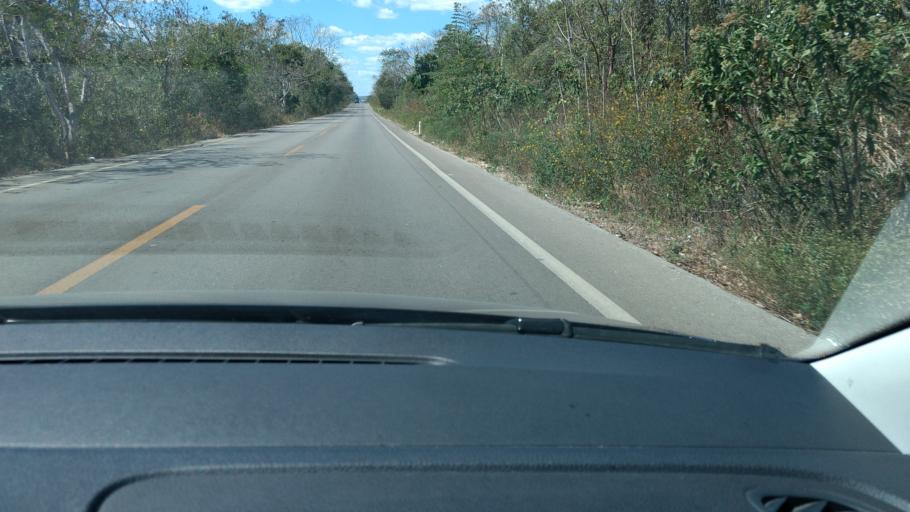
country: MX
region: Yucatan
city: Tzucacab
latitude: 20.0812
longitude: -89.0687
